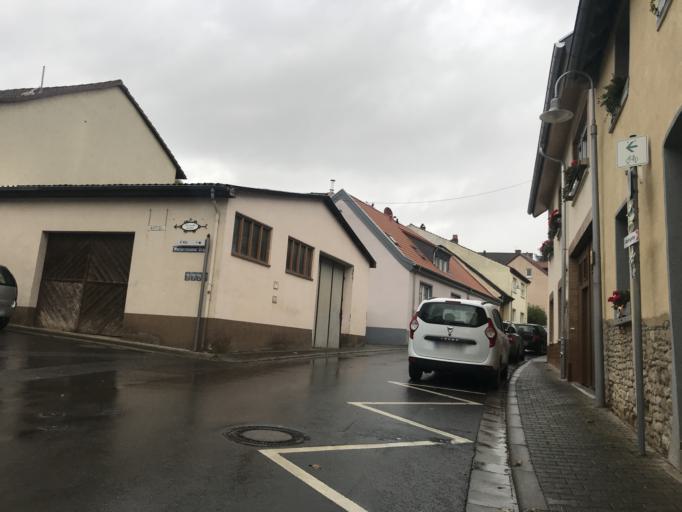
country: DE
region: Rheinland-Pfalz
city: Schwabenheim
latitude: 49.9336
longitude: 8.0986
